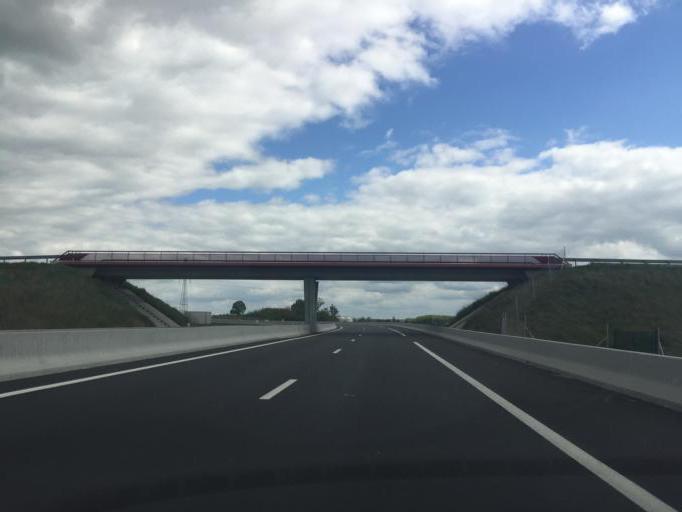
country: FR
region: Auvergne
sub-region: Departement de l'Allier
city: Varennes-sur-Allier
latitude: 46.3074
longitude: 3.3958
